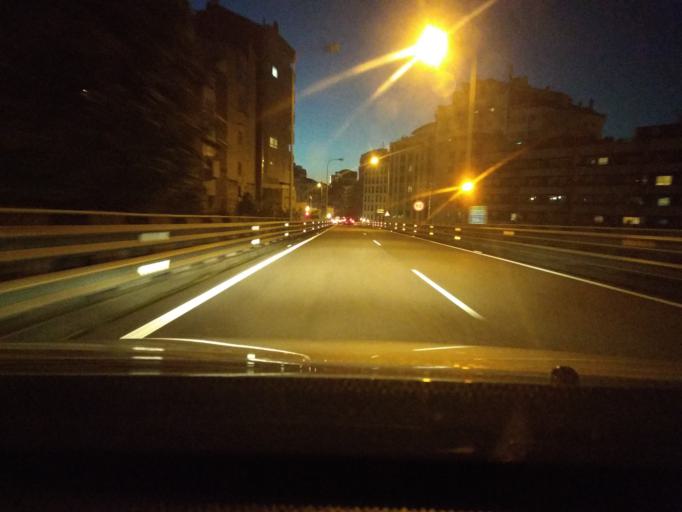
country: ES
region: Galicia
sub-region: Provincia de Pontevedra
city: Vigo
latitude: 42.2354
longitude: -8.7151
